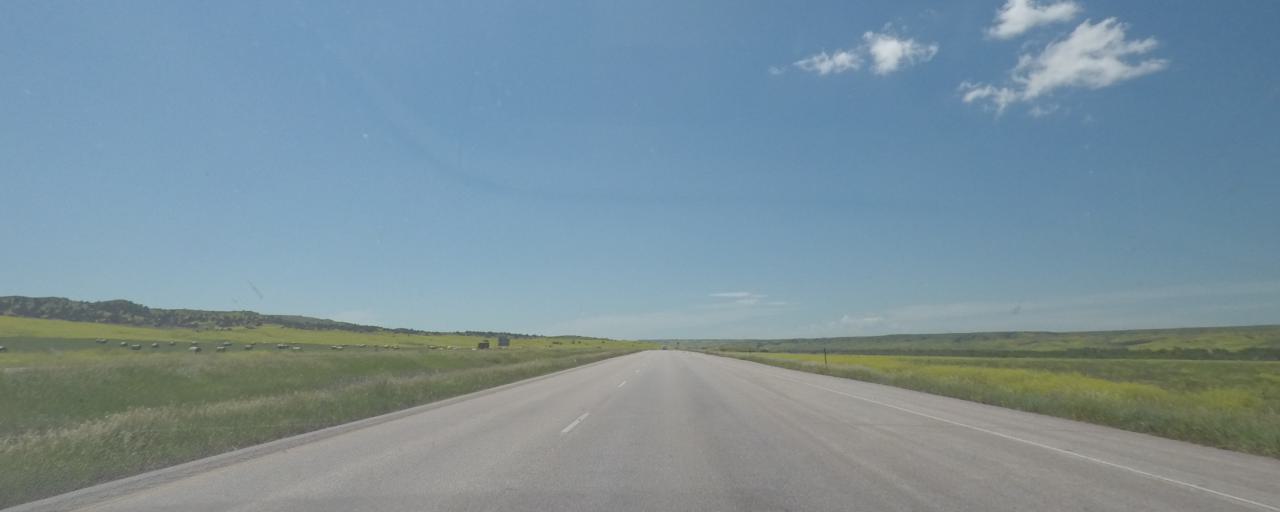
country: US
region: South Dakota
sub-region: Pennington County
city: Box Elder
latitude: 44.0678
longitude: -102.3941
